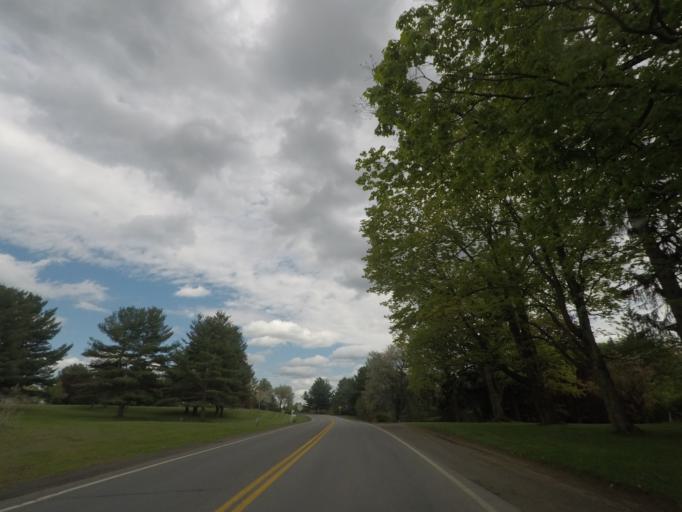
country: US
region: New York
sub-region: Albany County
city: Voorheesville
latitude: 42.6805
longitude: -73.9251
